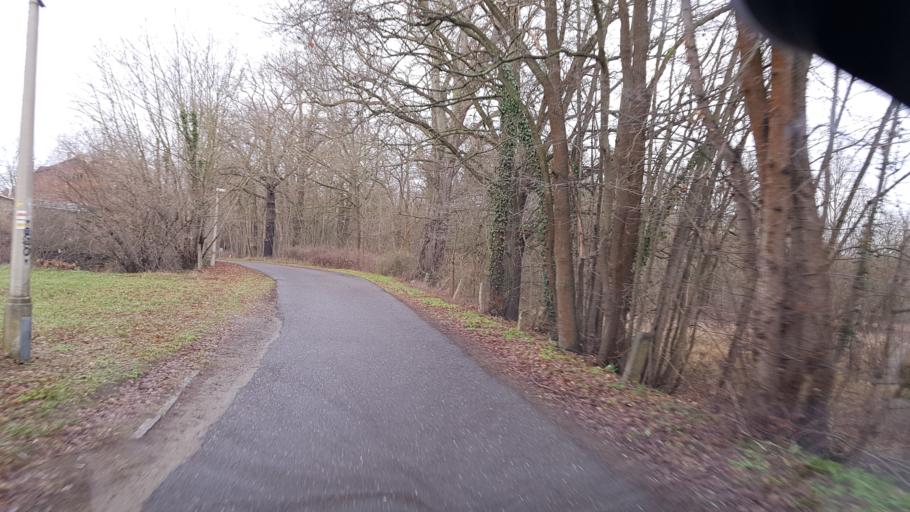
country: DE
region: Brandenburg
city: Altdobern
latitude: 51.6516
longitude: 14.0101
